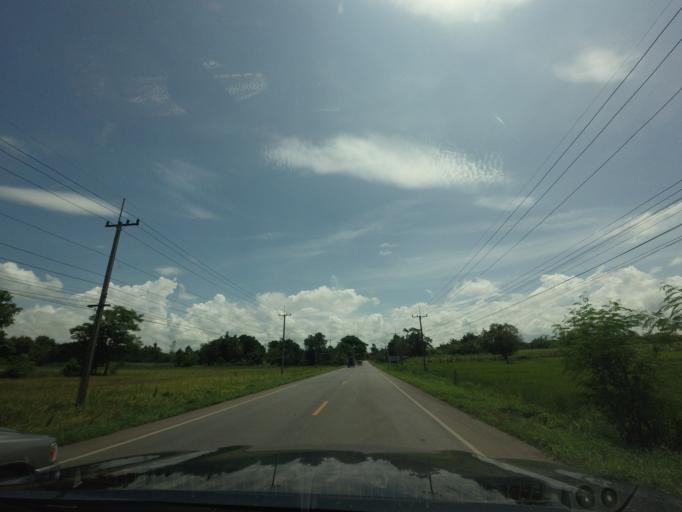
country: TH
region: Changwat Udon Thani
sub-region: Amphoe Ban Phue
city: Ban Phue
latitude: 17.7066
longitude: 102.4267
